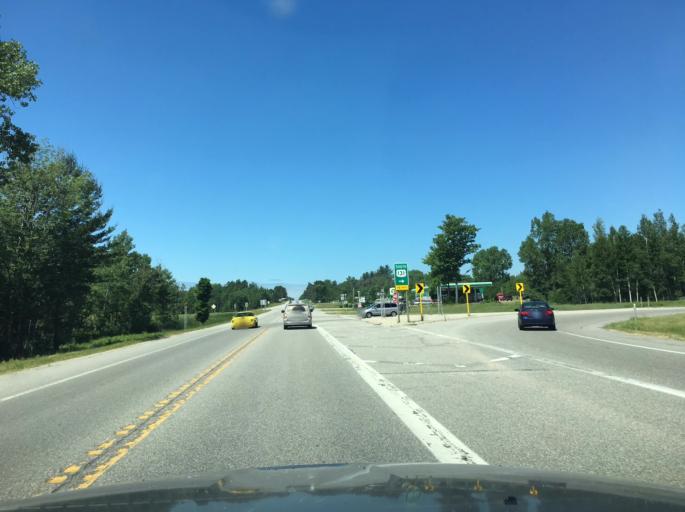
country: US
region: Michigan
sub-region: Osceola County
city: Reed City
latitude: 43.8875
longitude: -85.5310
